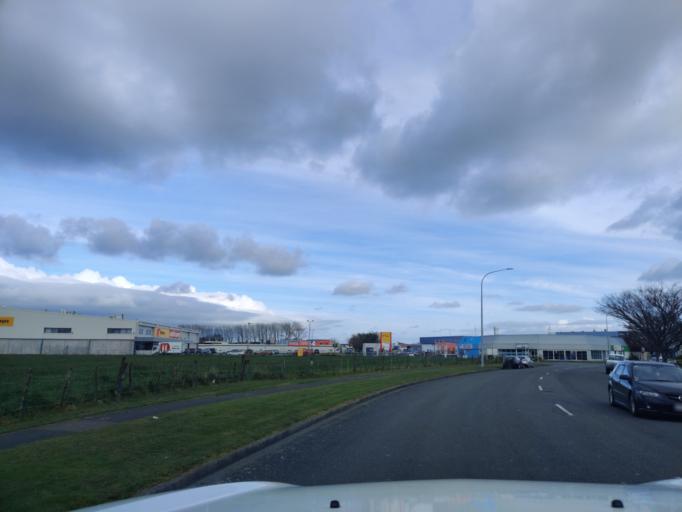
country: NZ
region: Manawatu-Wanganui
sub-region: Palmerston North City
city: Palmerston North
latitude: -40.3381
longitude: 175.6023
